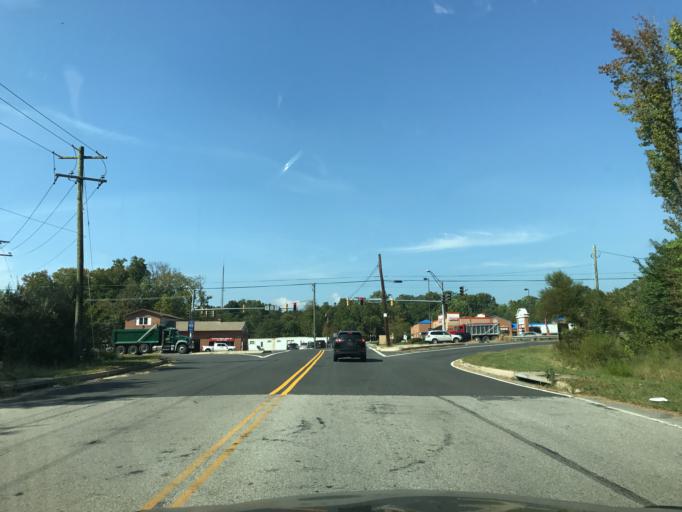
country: US
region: Maryland
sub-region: Cecil County
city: Perryville
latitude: 39.5705
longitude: -76.0664
